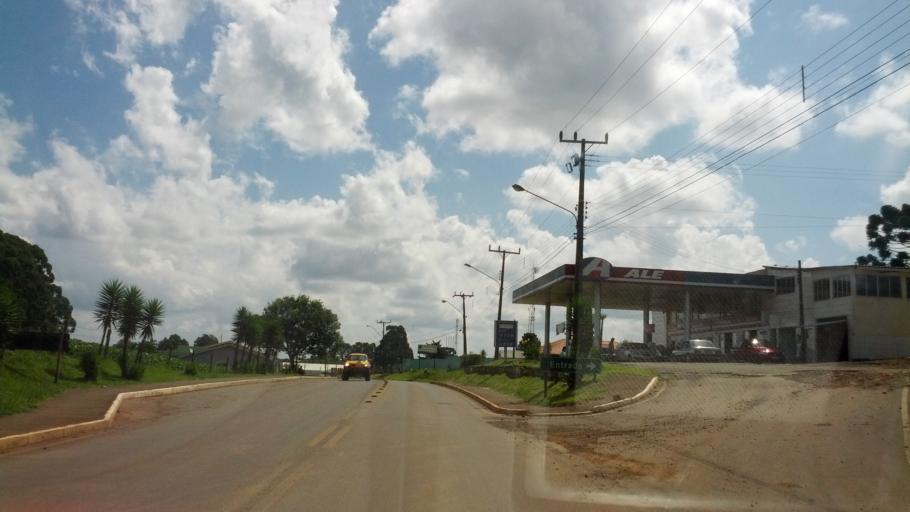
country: BR
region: Rio Grande do Sul
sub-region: Vacaria
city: Estrela
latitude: -27.7969
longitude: -50.8683
